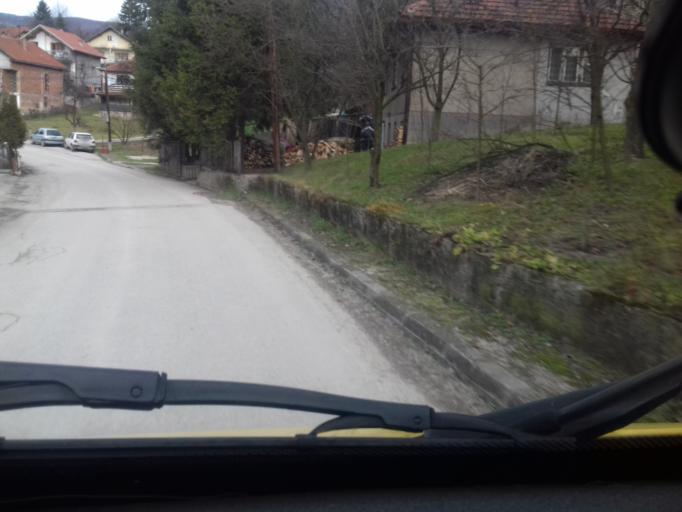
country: BA
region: Federation of Bosnia and Herzegovina
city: Zenica
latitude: 44.2361
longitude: 17.9122
